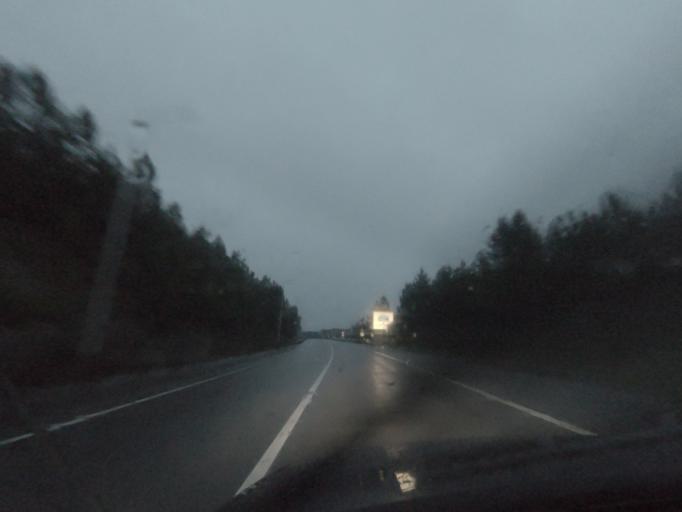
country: PT
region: Vila Real
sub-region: Vila Real
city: Vila Real
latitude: 41.2748
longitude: -7.6974
